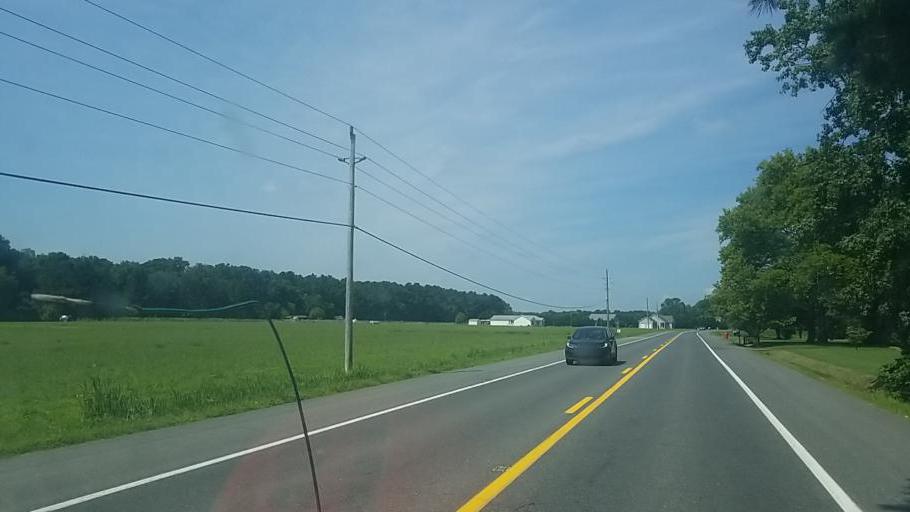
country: US
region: Delaware
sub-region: Sussex County
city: Bridgeville
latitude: 38.8240
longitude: -75.6385
